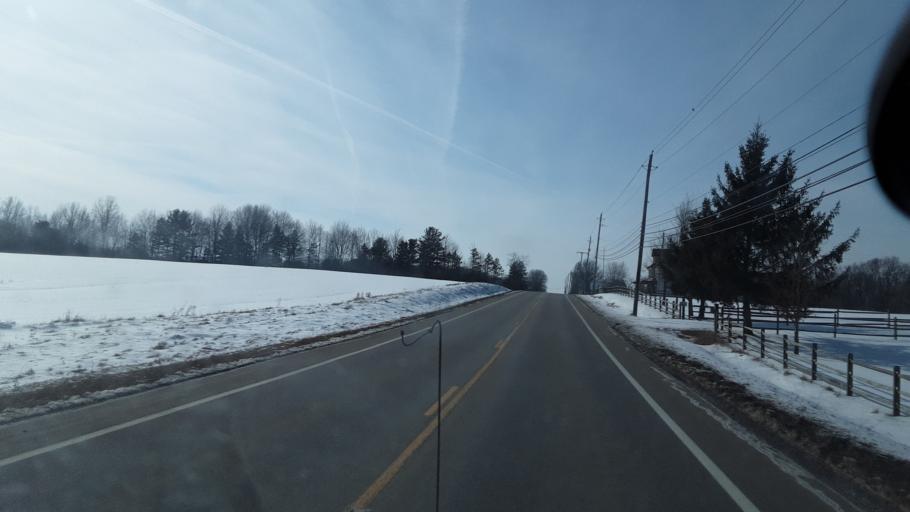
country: US
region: Ohio
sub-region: Mahoning County
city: Canfield
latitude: 41.0245
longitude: -80.8218
